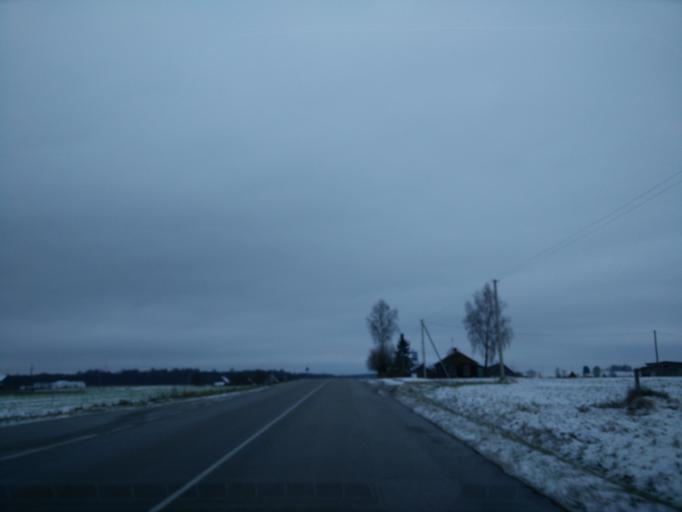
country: LT
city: Tytuveneliai
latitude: 55.5091
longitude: 23.2885
